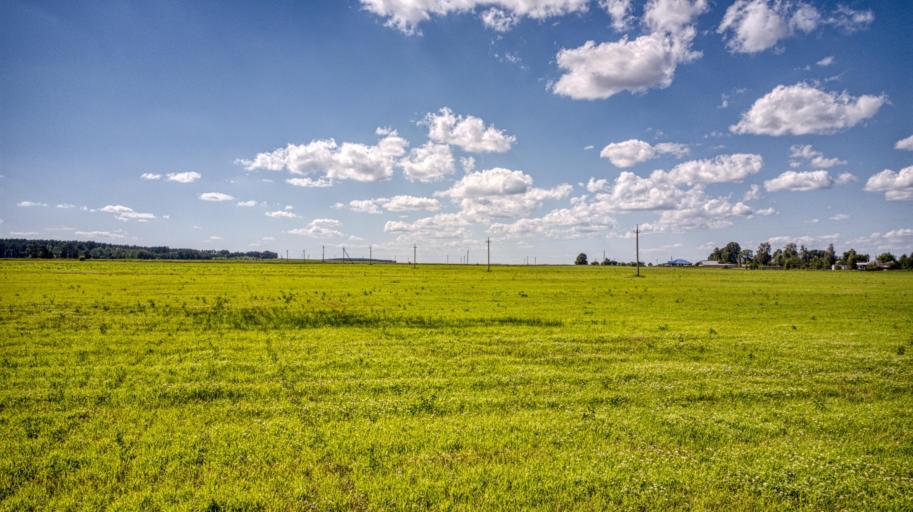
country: BY
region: Brest
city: Kamyanyets
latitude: 52.4011
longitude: 23.8919
